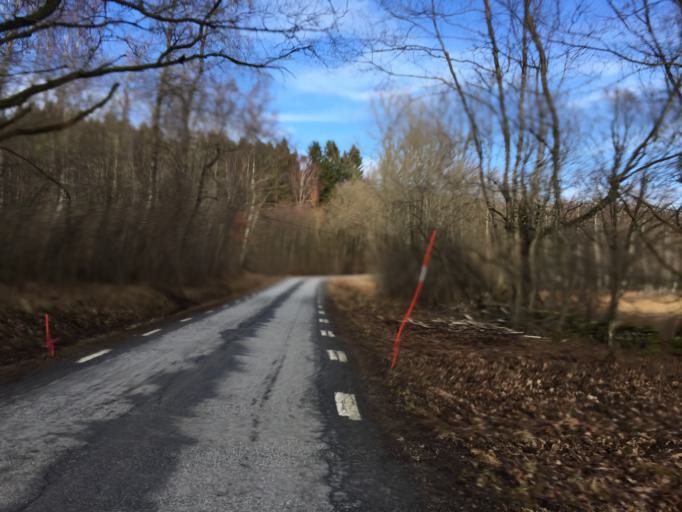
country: SE
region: Vaestra Goetaland
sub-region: Kungalvs Kommun
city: Kungalv
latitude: 57.9294
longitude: 11.9528
